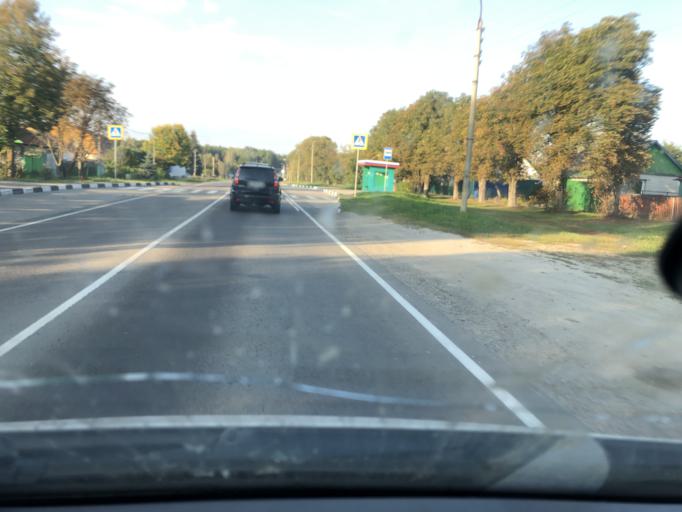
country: RU
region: Kaluga
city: Peremyshl'
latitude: 54.3809
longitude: 36.1997
